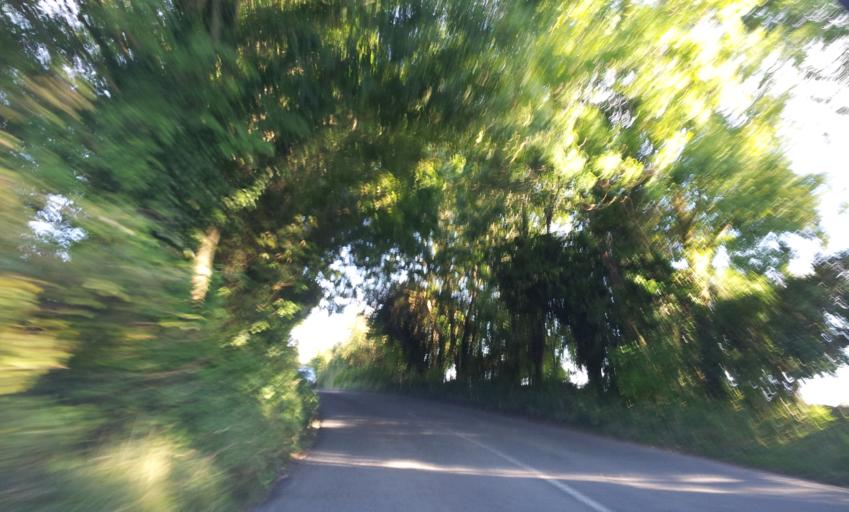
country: IE
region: Munster
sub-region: An Clar
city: Ennis
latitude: 52.9527
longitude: -9.0701
